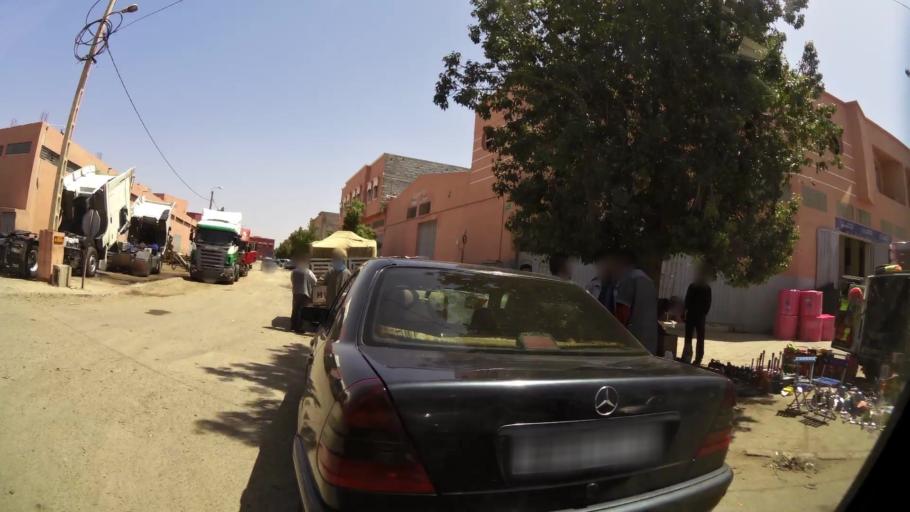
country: MA
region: Souss-Massa-Draa
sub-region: Inezgane-Ait Mellou
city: Inezgane
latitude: 30.3379
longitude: -9.4838
